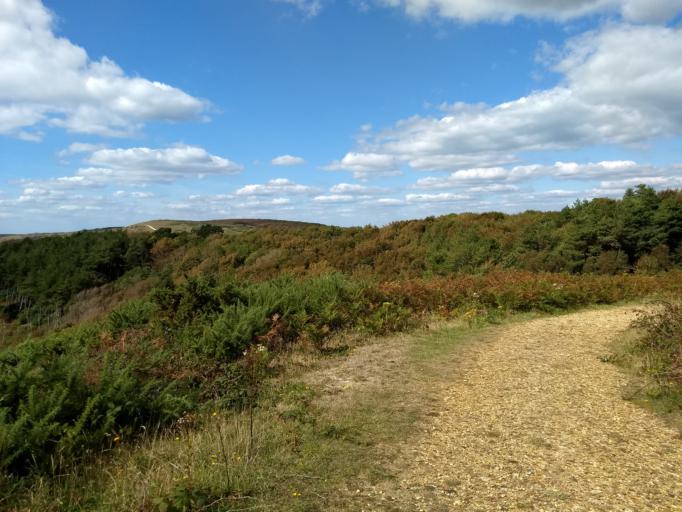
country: GB
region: England
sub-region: Isle of Wight
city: Shalfleet
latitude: 50.6576
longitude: -1.4338
